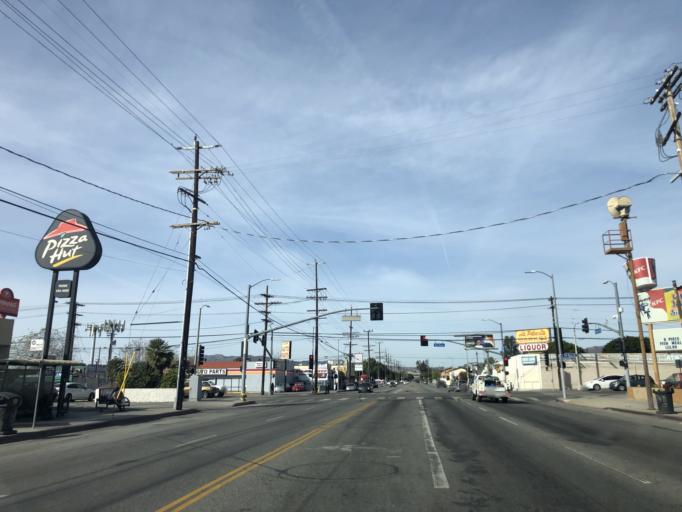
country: US
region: California
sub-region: Los Angeles County
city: San Fernando
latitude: 34.2582
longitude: -118.4315
